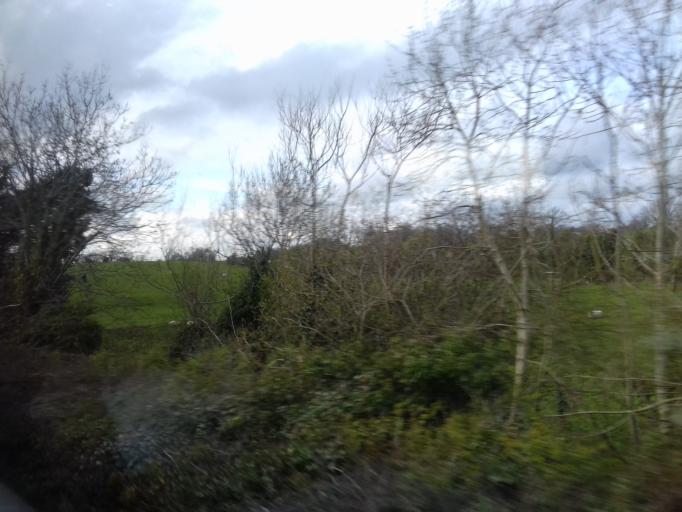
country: IE
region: Leinster
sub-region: An Mhi
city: Enfield
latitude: 53.4133
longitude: -6.8576
